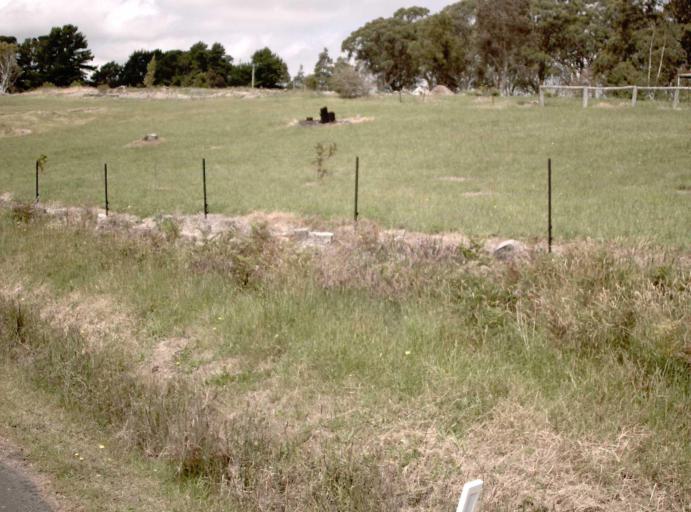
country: AU
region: Victoria
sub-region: Latrobe
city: Traralgon
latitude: -38.3708
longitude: 146.6907
